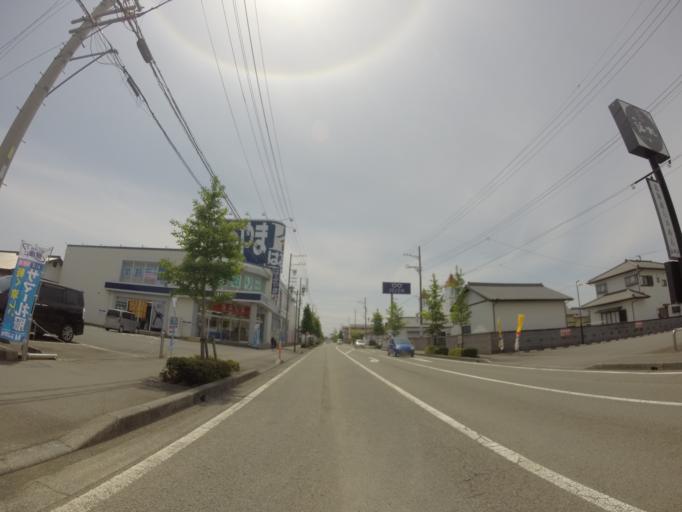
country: JP
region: Shizuoka
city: Yaizu
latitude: 34.8479
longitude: 138.3083
